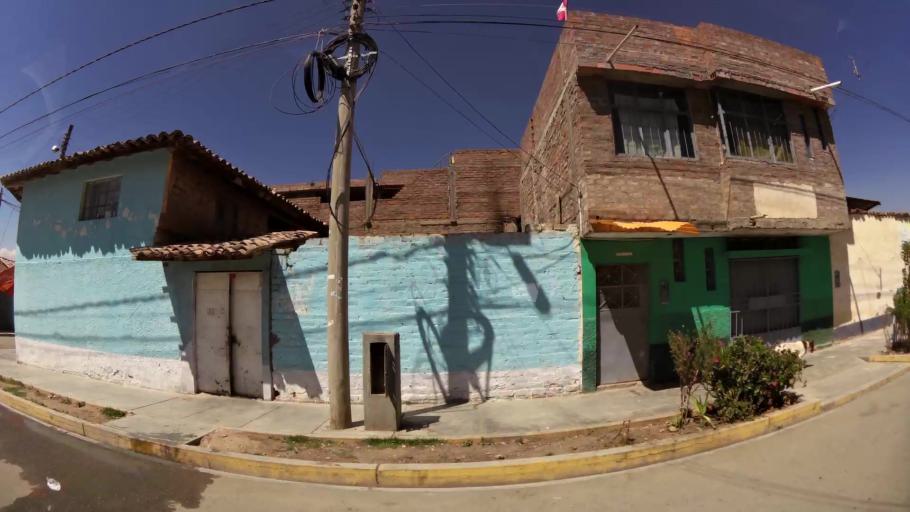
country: PE
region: Junin
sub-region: Provincia de Jauja
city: Jauja
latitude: -11.7727
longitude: -75.4945
